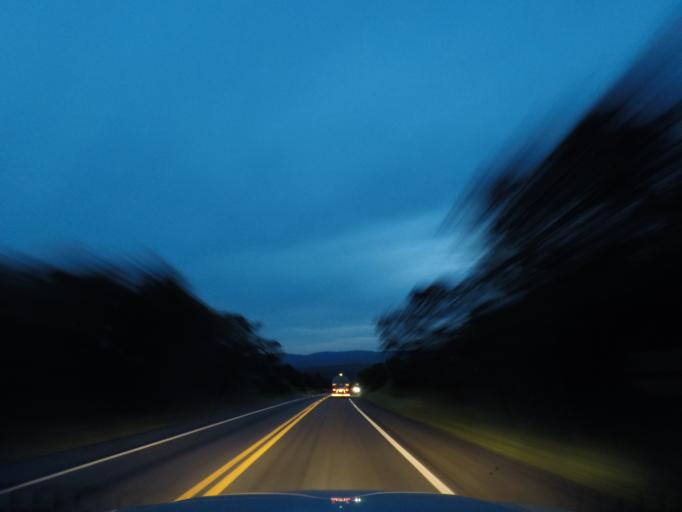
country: BR
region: Bahia
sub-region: Andarai
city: Vera Cruz
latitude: -12.4955
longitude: -41.3167
